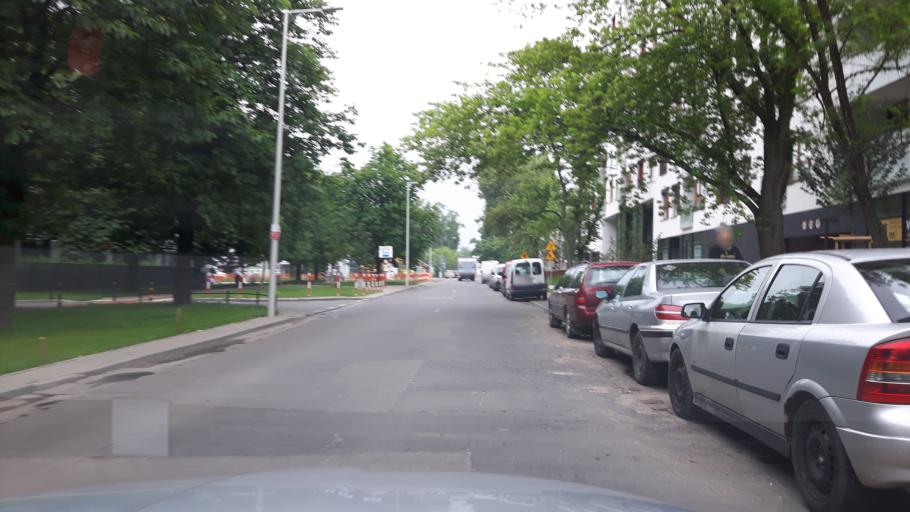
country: PL
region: Masovian Voivodeship
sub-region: Warszawa
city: Zoliborz
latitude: 52.2591
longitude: 20.9699
